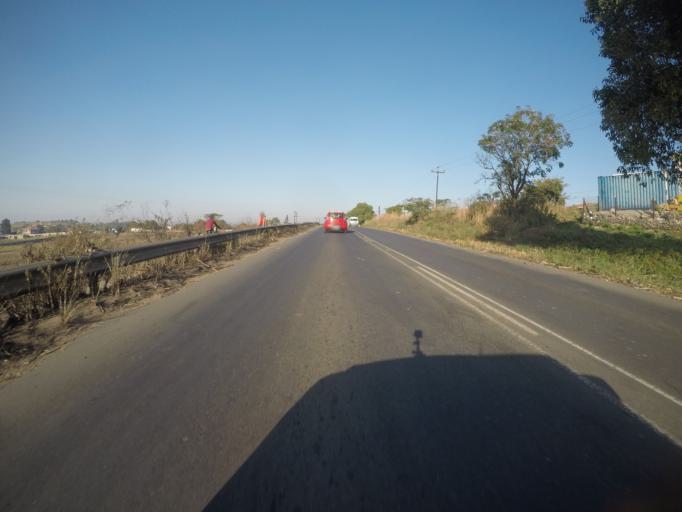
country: ZA
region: KwaZulu-Natal
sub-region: iLembe District Municipality
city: Stanger
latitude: -29.4088
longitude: 31.2470
